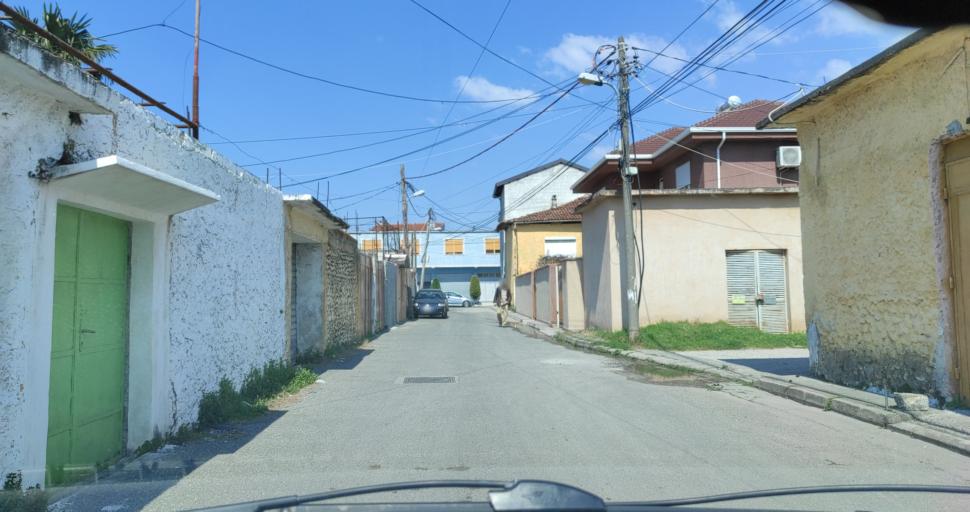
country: AL
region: Shkoder
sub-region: Rrethi i Shkodres
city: Shkoder
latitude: 42.0732
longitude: 19.5113
